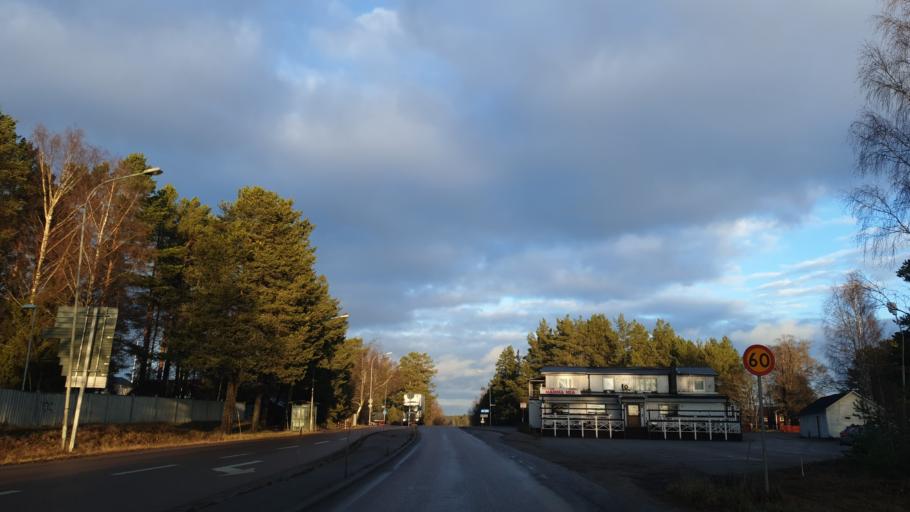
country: SE
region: Gaevleborg
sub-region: Hudiksvalls Kommun
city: Hudiksvall
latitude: 61.7521
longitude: 17.1203
